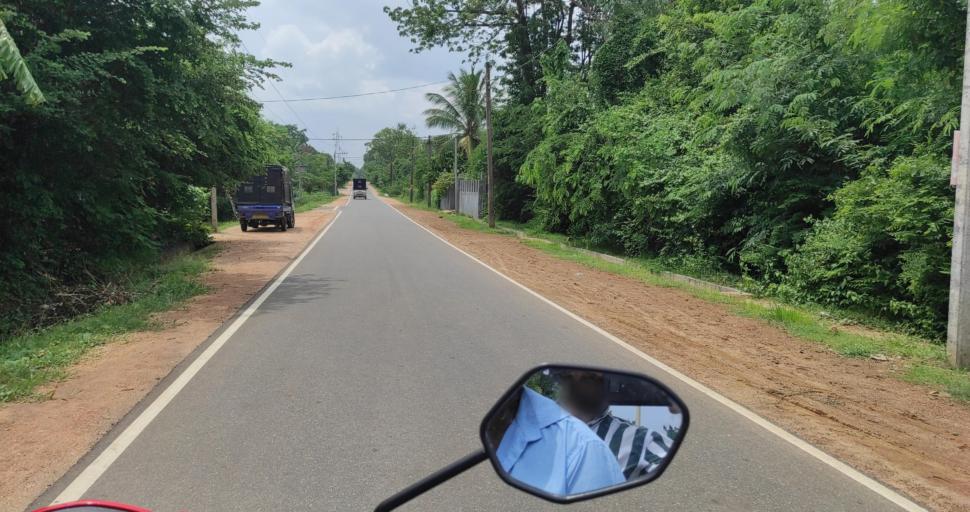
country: LK
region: Eastern Province
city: Trincomalee
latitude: 8.3775
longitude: 81.0144
